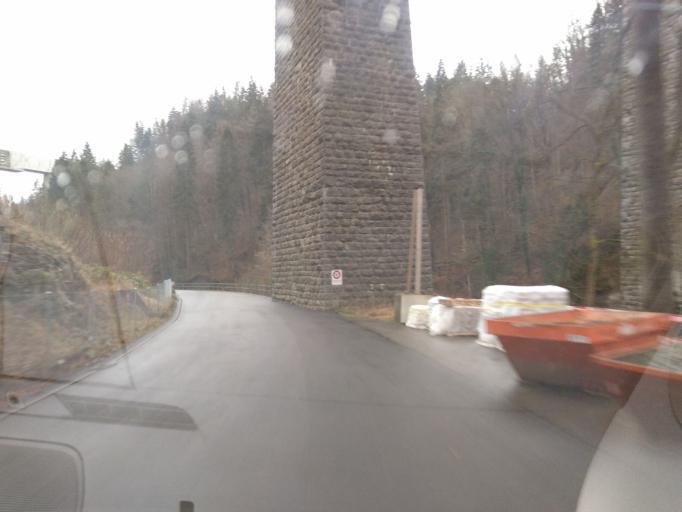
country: CH
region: Appenzell Ausserrhoden
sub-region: Bezirk Hinterland
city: Herisau
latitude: 47.4041
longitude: 9.3224
